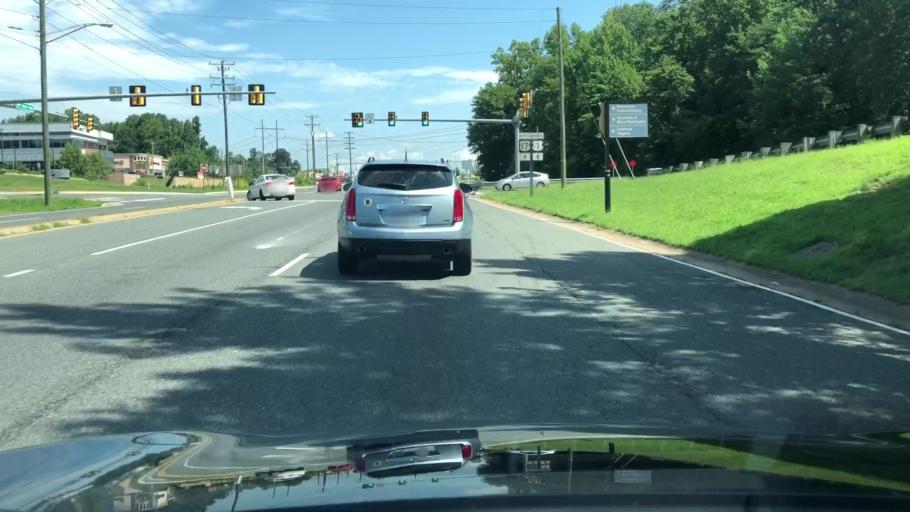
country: US
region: Virginia
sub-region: City of Fredericksburg
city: Fredericksburg
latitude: 38.2987
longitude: -77.4827
